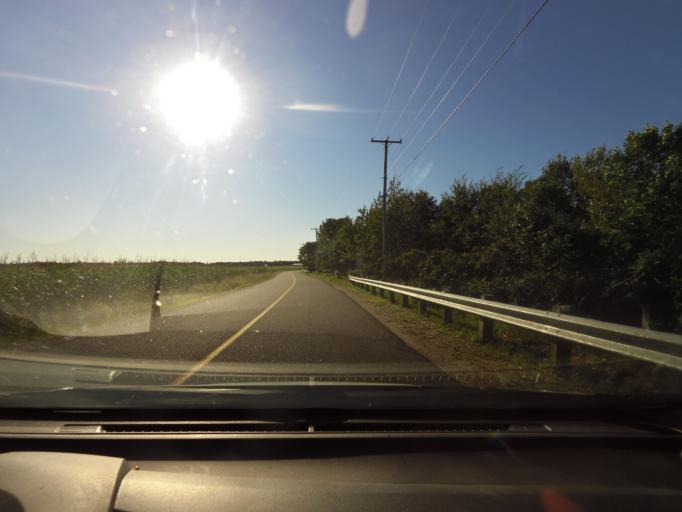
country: CA
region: Quebec
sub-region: Mauricie
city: Becancour
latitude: 46.5537
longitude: -72.3636
